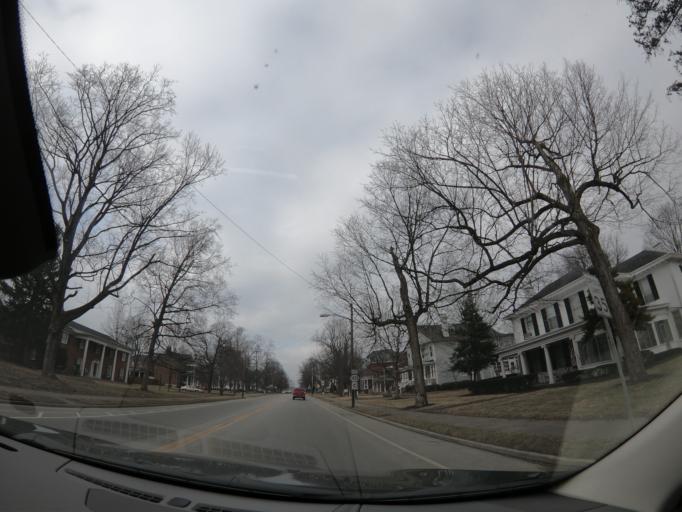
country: US
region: Kentucky
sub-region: Nelson County
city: Bardstown
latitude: 37.8136
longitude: -85.4655
